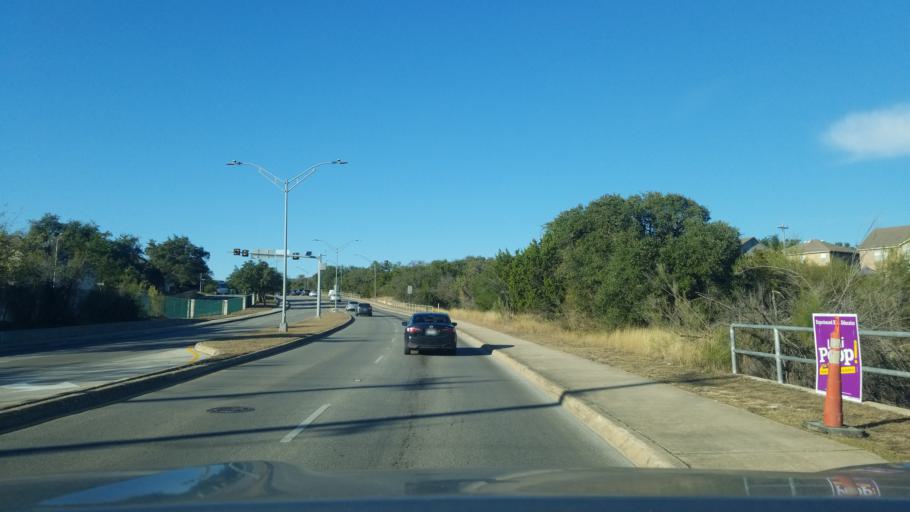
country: US
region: Texas
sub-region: Bexar County
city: Hollywood Park
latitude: 29.6316
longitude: -98.4811
